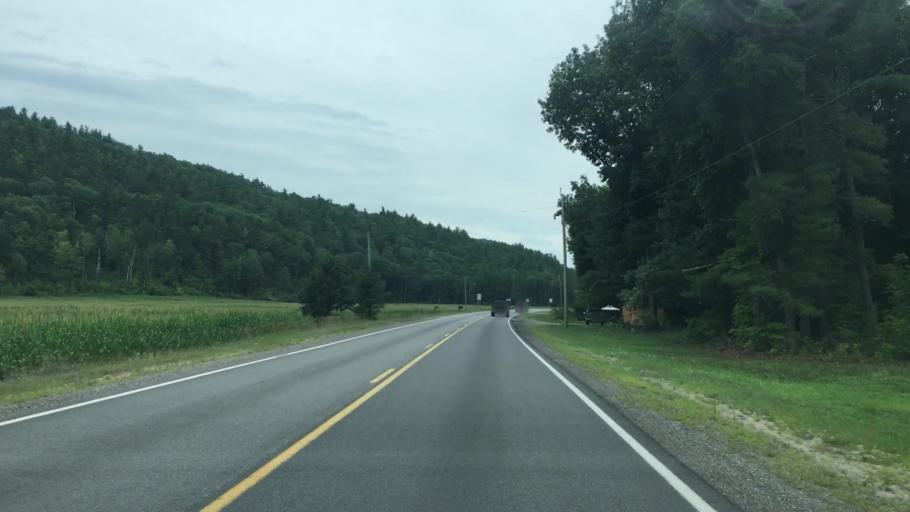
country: US
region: New York
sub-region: Clinton County
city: Peru
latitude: 44.5145
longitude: -73.5814
